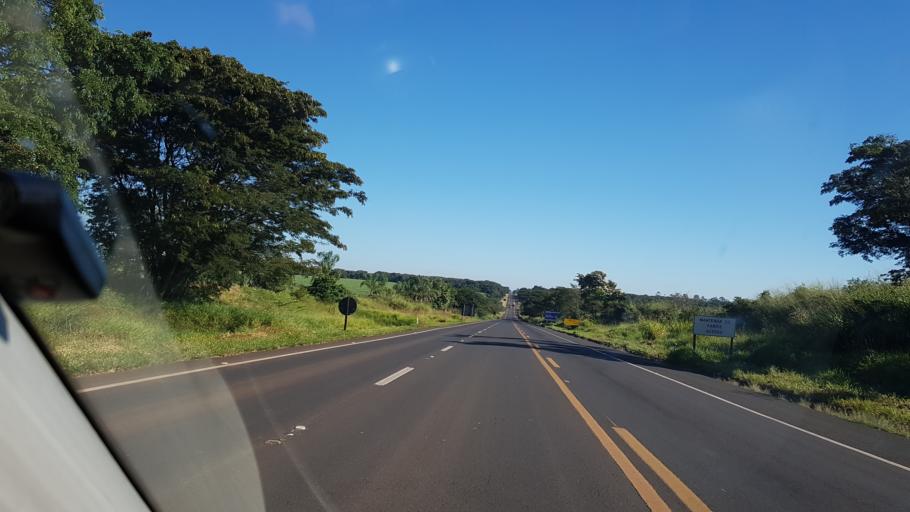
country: BR
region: Sao Paulo
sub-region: Assis
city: Assis
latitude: -22.5927
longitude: -50.4906
